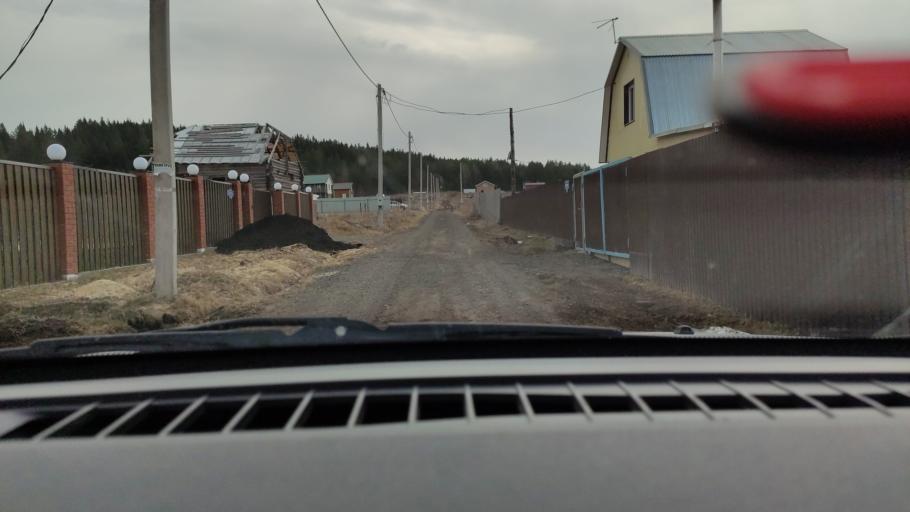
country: RU
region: Perm
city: Kultayevo
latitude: 57.8946
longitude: 56.0167
